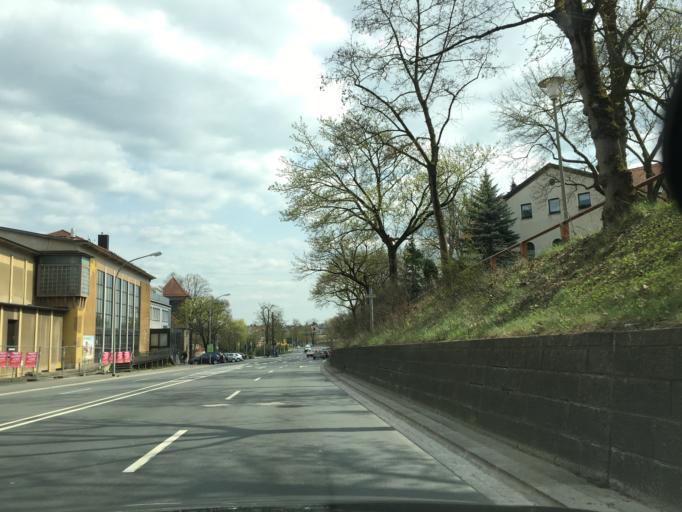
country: DE
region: Bavaria
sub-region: Upper Palatinate
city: Amberg
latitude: 49.4427
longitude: 11.8537
